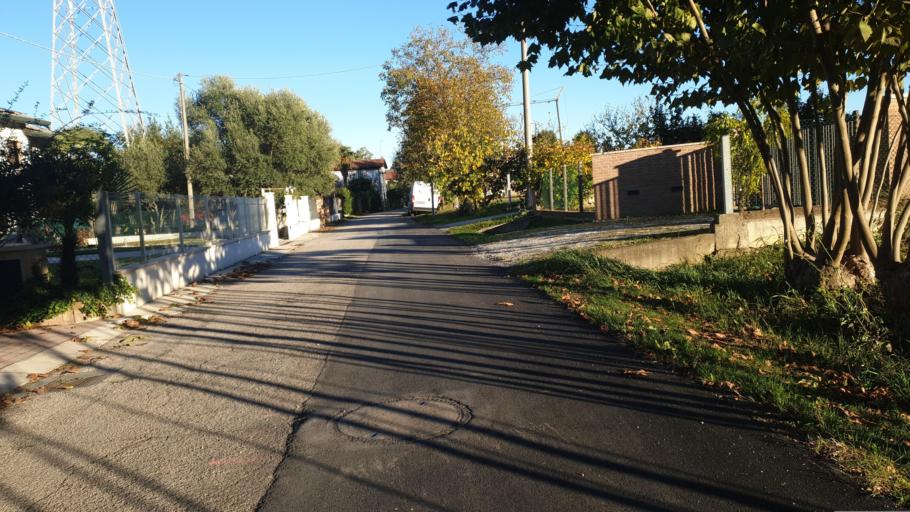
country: IT
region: Veneto
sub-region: Provincia di Venezia
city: Scaltenigo
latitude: 45.4683
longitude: 12.0945
